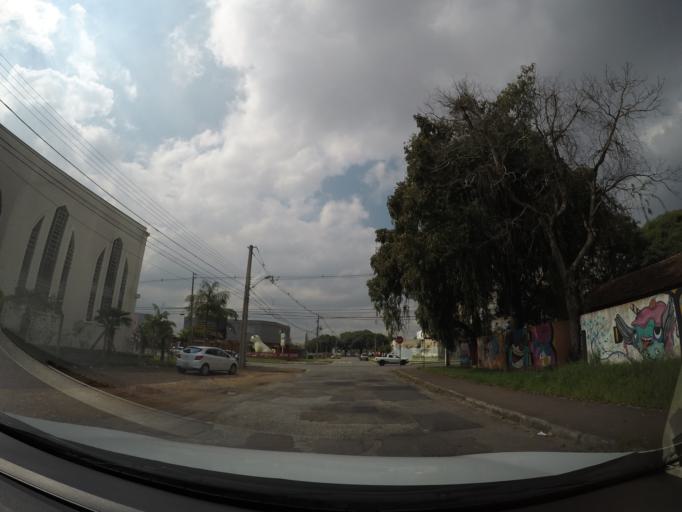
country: BR
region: Parana
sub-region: Sao Jose Dos Pinhais
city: Sao Jose dos Pinhais
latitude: -25.4944
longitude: -49.2427
